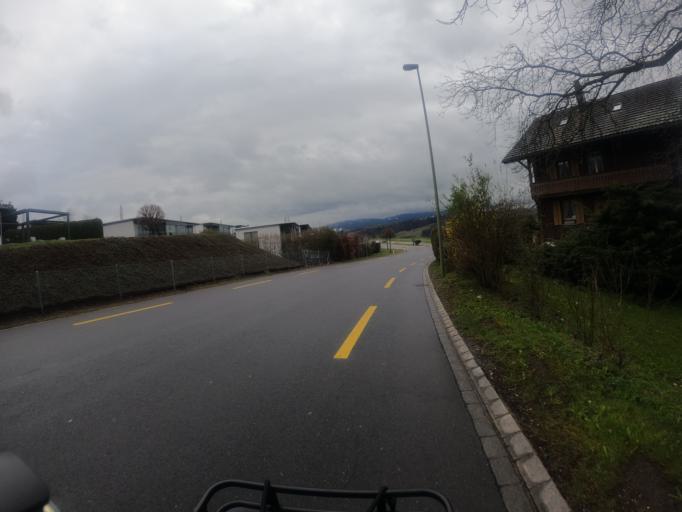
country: CH
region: Zurich
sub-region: Bezirk Affoltern
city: Hausen am Albis / Hausen (Dorf)
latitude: 47.2245
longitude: 8.5511
